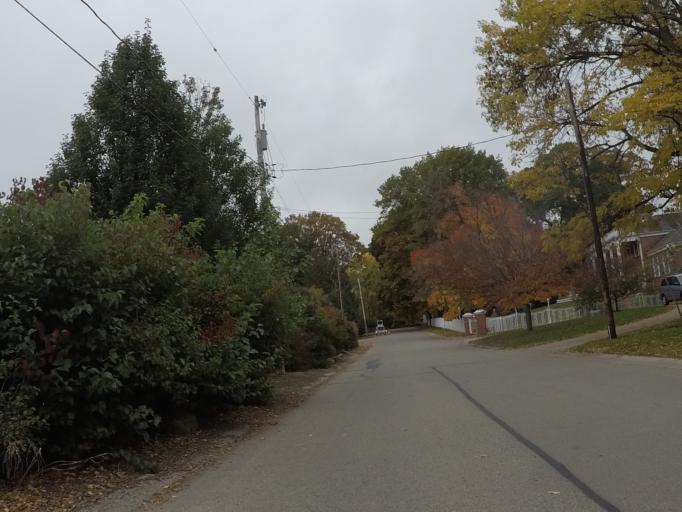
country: US
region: Wisconsin
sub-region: Dane County
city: Maple Bluff
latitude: 43.1045
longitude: -89.3664
